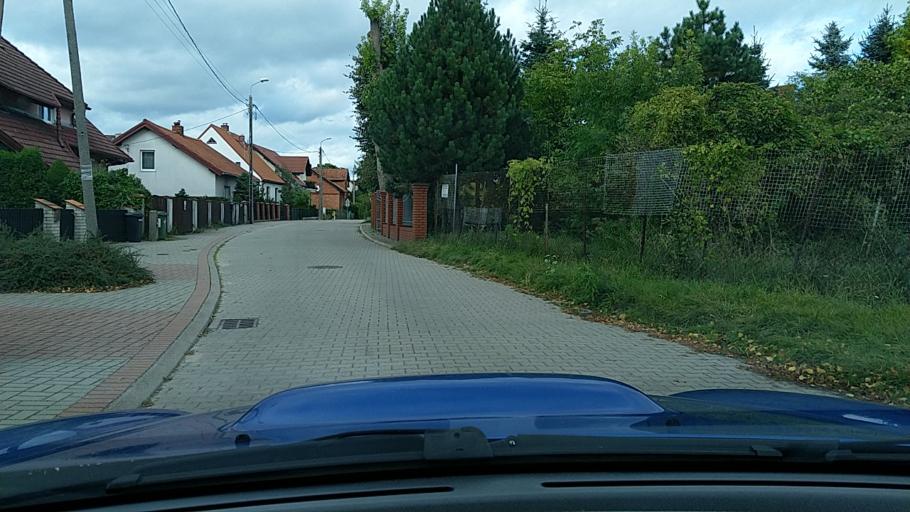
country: PL
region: Warmian-Masurian Voivodeship
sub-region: Olsztyn
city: Kortowo
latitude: 53.7657
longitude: 20.4205
